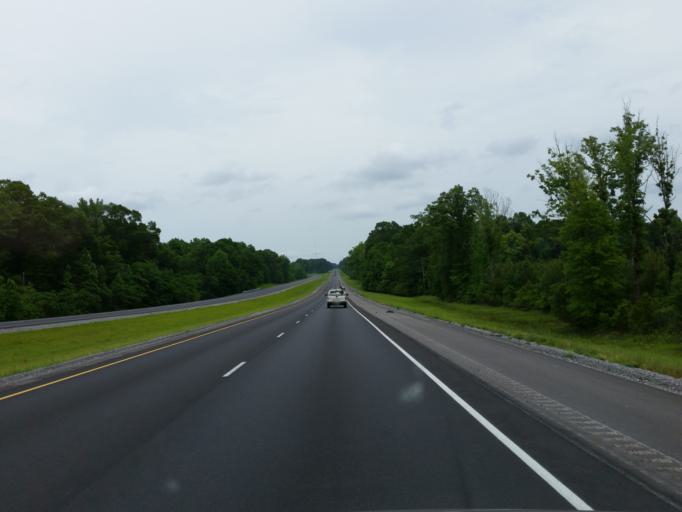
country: US
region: Mississippi
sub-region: Jones County
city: Sharon
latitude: 31.9354
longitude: -88.9937
